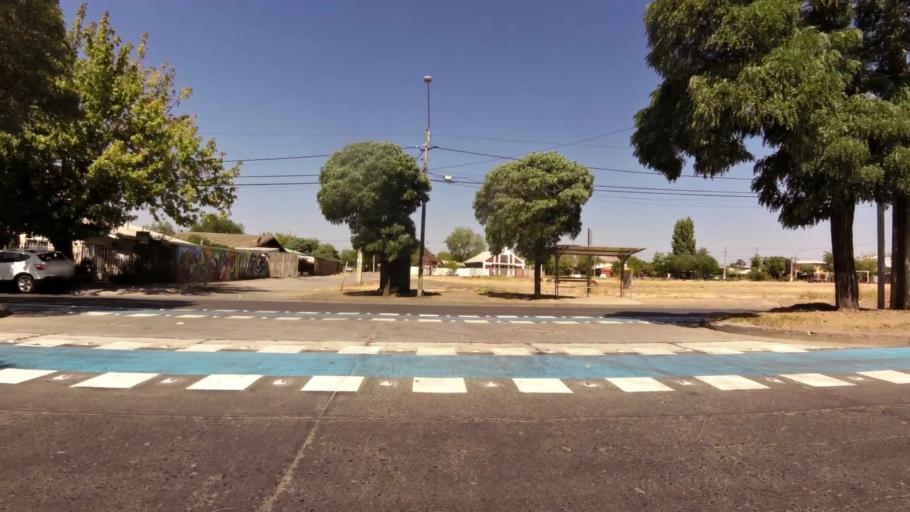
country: CL
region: Maule
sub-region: Provincia de Talca
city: Talca
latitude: -35.4429
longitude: -71.6533
